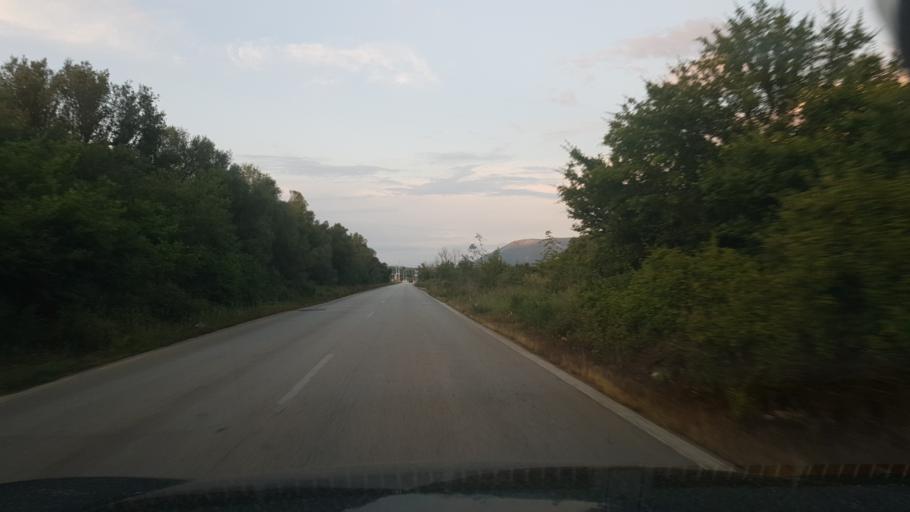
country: GR
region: West Greece
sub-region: Nomos Aitolias kai Akarnanias
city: Vonitsa
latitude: 38.8873
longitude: 20.8467
